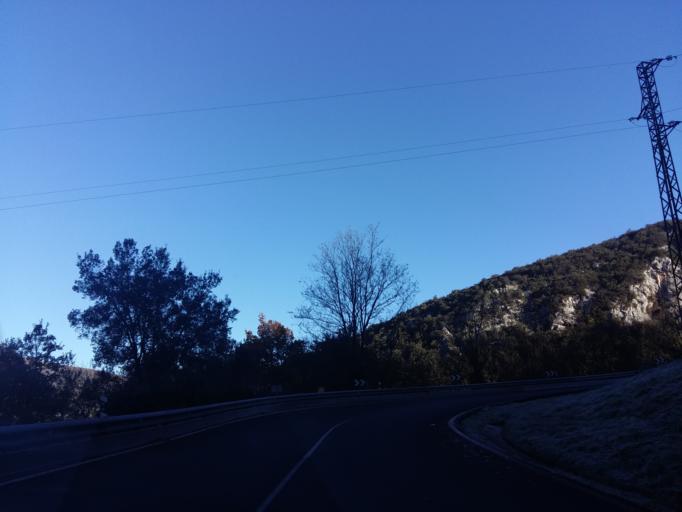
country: ES
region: Cantabria
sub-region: Provincia de Cantabria
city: Ramales de la Victoria
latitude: 43.2459
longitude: -3.4597
